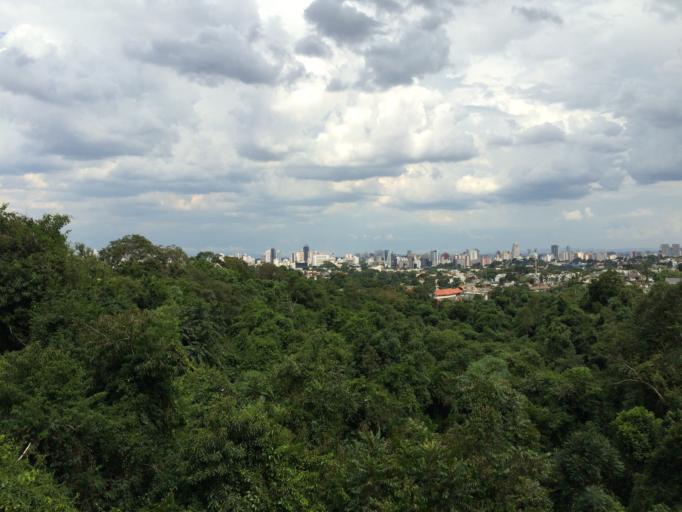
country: BR
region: Parana
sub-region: Curitiba
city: Curitiba
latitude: -25.4045
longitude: -49.2877
